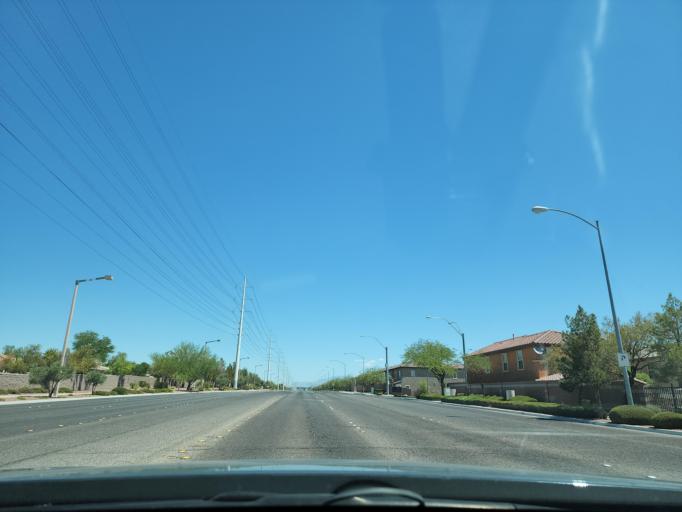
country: US
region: Nevada
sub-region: Clark County
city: Summerlin South
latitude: 36.0912
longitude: -115.3156
